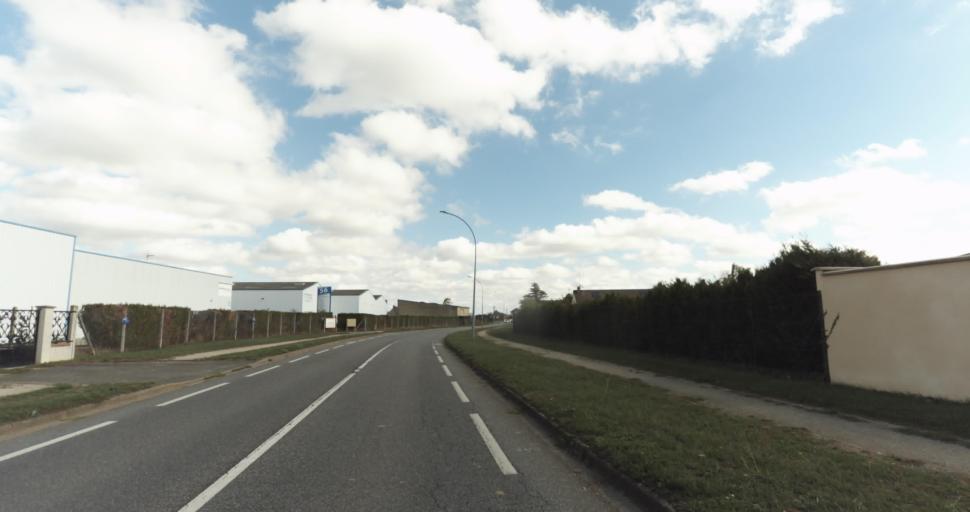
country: FR
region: Centre
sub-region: Departement d'Eure-et-Loir
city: Garnay
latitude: 48.7291
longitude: 1.3237
